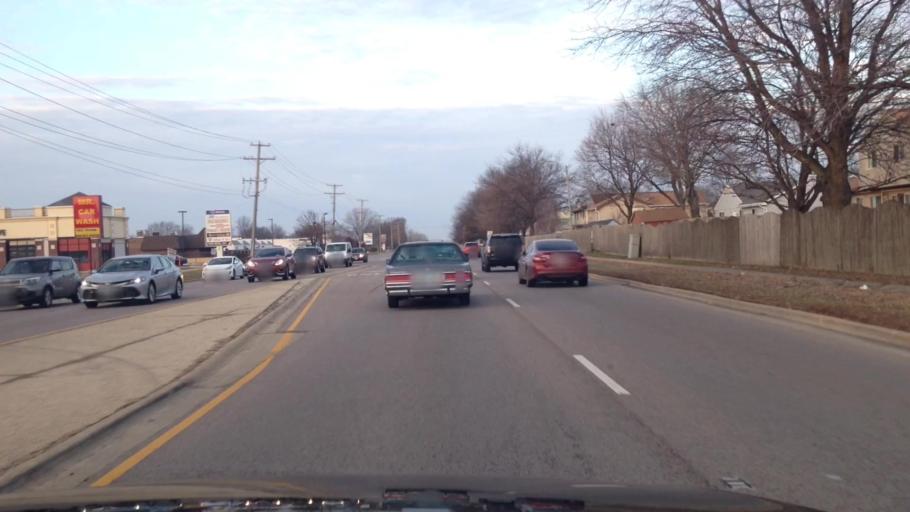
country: US
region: Illinois
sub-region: DuPage County
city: Hanover Park
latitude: 42.0321
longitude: -88.1445
